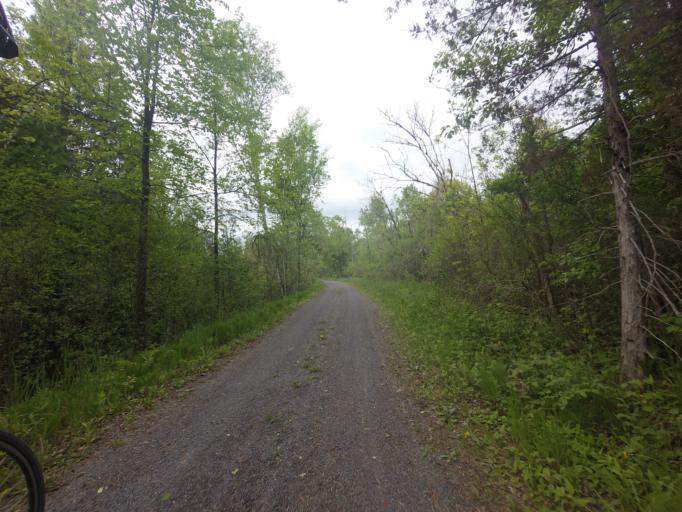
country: CA
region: Ontario
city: Kingston
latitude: 44.3841
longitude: -76.6386
